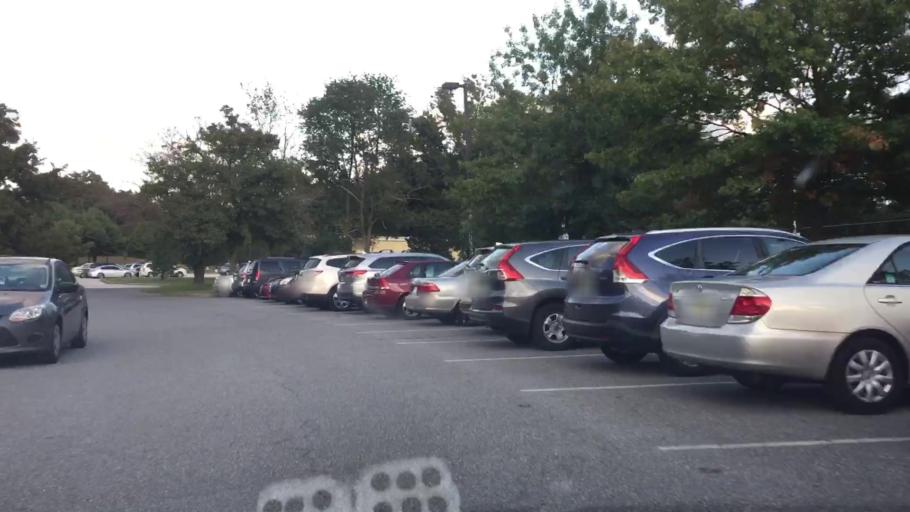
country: US
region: New Jersey
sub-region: Gloucester County
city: Pitman
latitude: 39.7411
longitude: -75.0940
